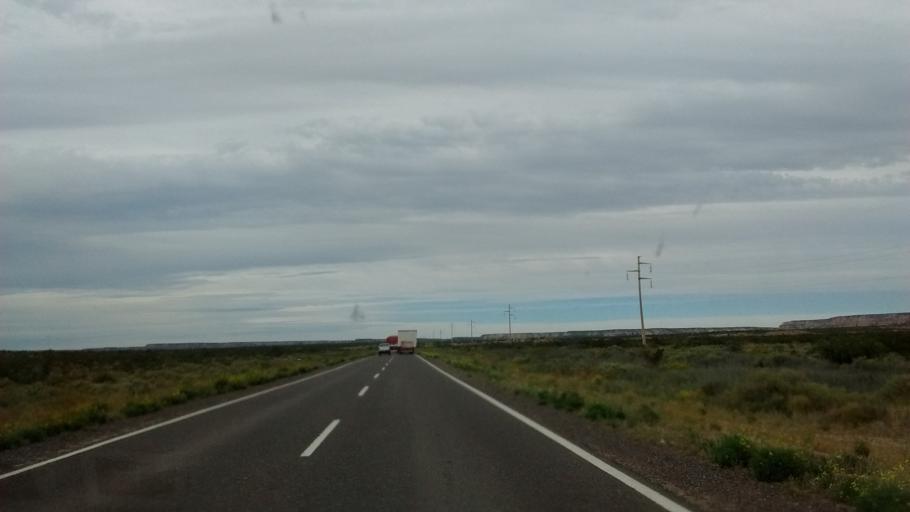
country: AR
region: Rio Negro
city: Catriel
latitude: -38.1361
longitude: -67.9370
